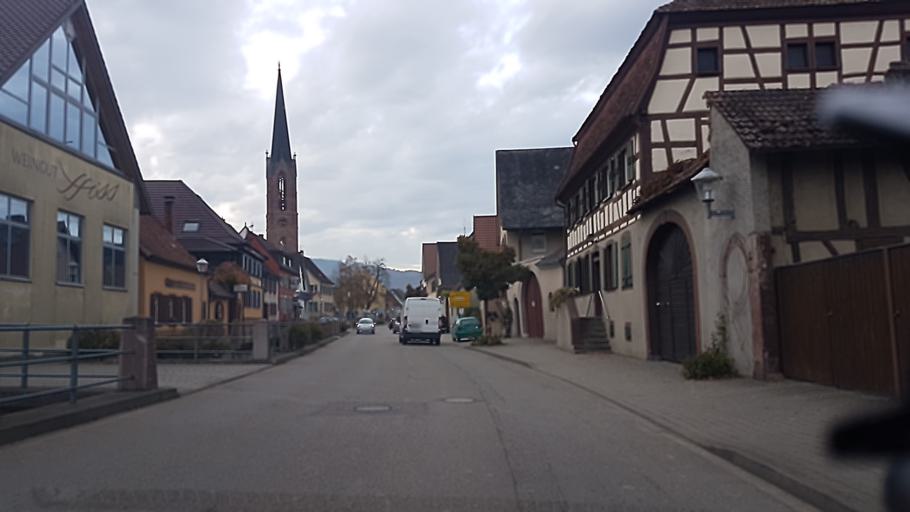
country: DE
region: Baden-Wuerttemberg
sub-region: Freiburg Region
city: Eichstetten
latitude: 48.0939
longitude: 7.7479
